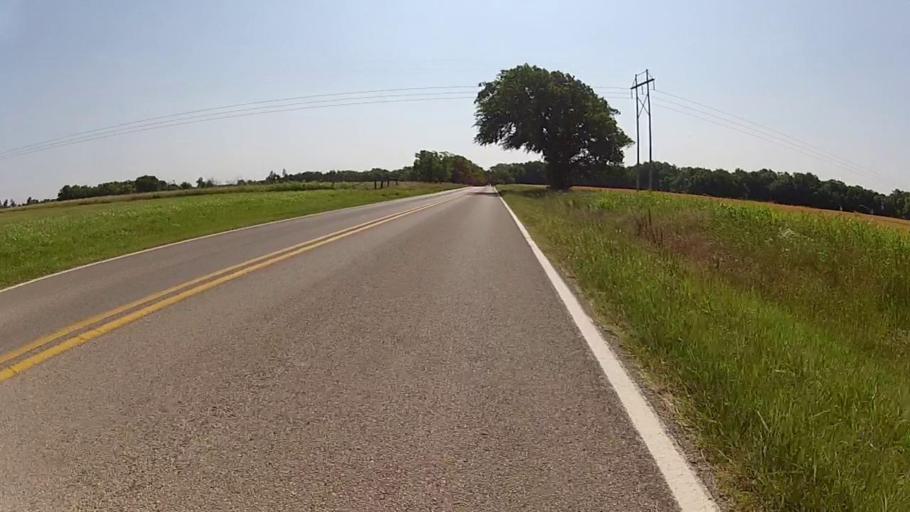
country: US
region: Kansas
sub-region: Montgomery County
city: Independence
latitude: 37.1930
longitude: -95.7385
